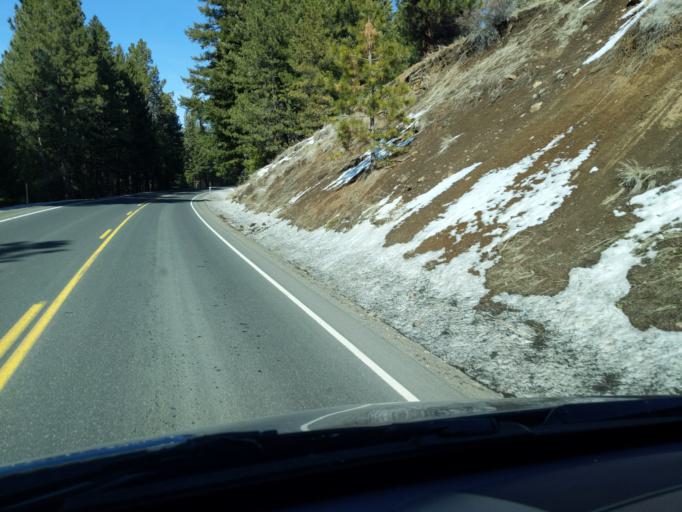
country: US
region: Oregon
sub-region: Grant County
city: John Day
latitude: 44.8844
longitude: -119.0142
